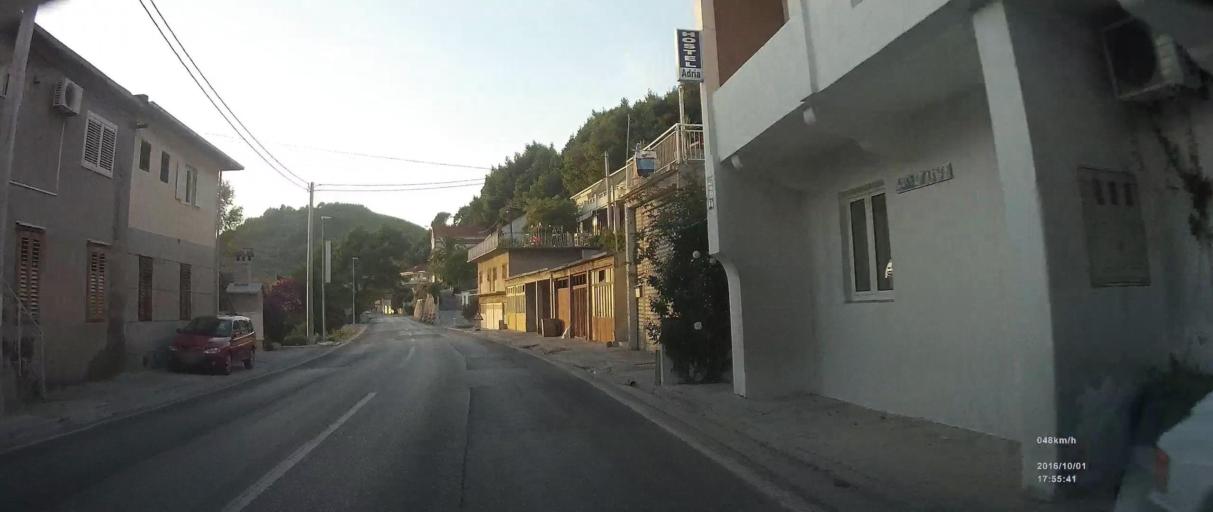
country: HR
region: Splitsko-Dalmatinska
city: Srinjine
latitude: 43.4636
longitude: 16.5905
